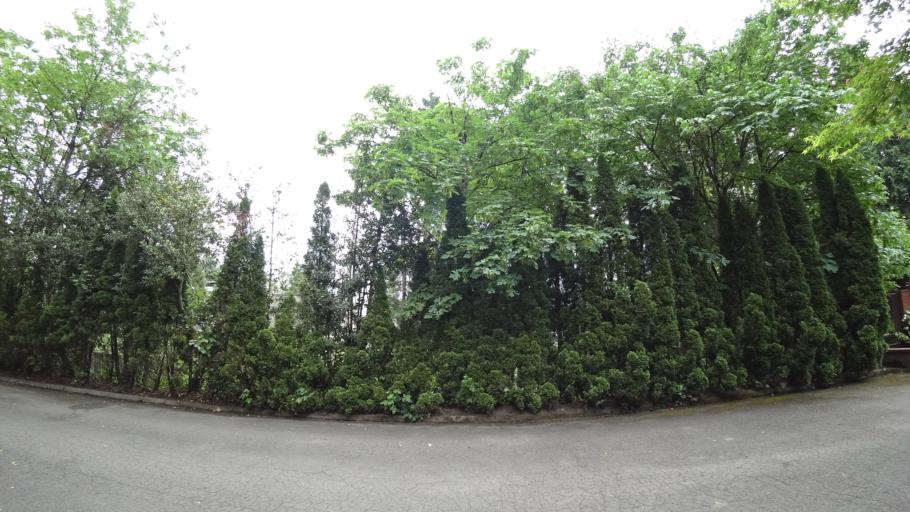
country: US
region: Oregon
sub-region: Clackamas County
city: Milwaukie
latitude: 45.4413
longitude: -122.6512
